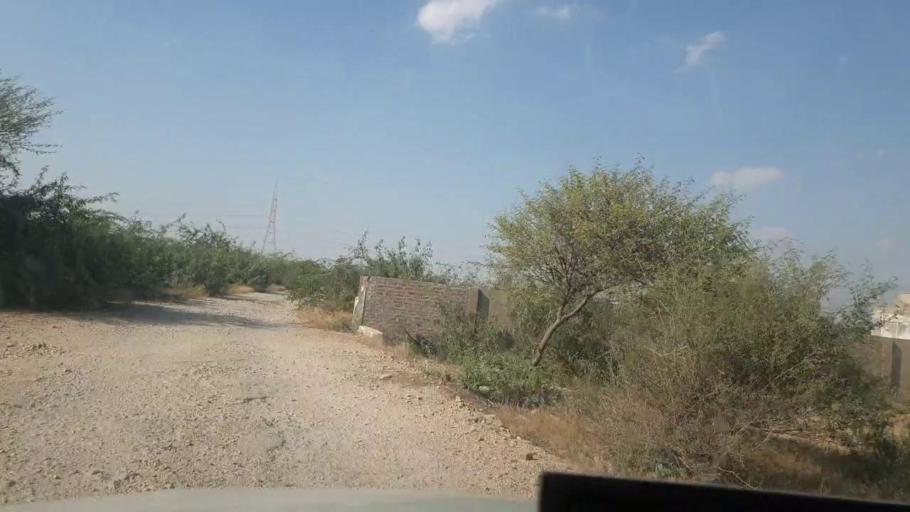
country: PK
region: Sindh
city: Daro Mehar
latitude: 25.0683
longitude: 68.0988
